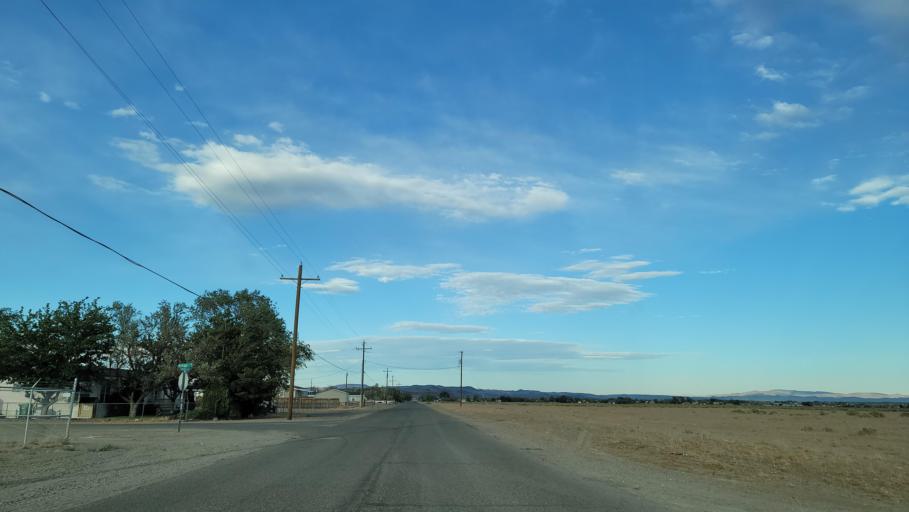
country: US
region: Nevada
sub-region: Lyon County
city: Silver Springs
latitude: 39.3899
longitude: -119.2493
